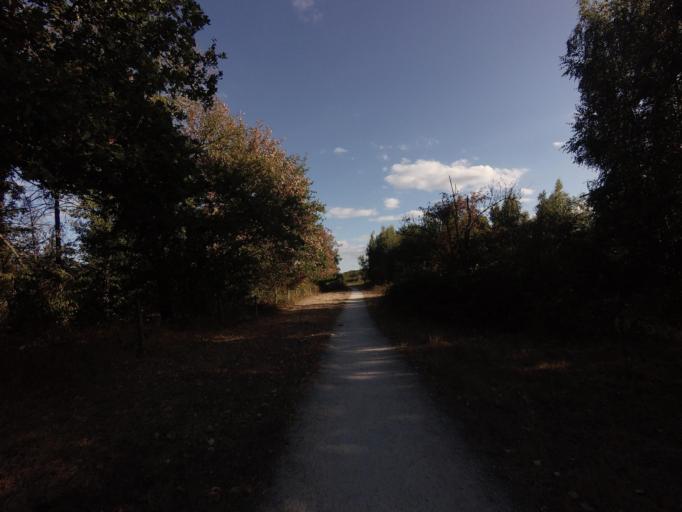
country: NL
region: North Brabant
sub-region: Gemeente Mill en Sint Hubert
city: Wilbertoord
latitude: 51.6994
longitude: 5.7536
